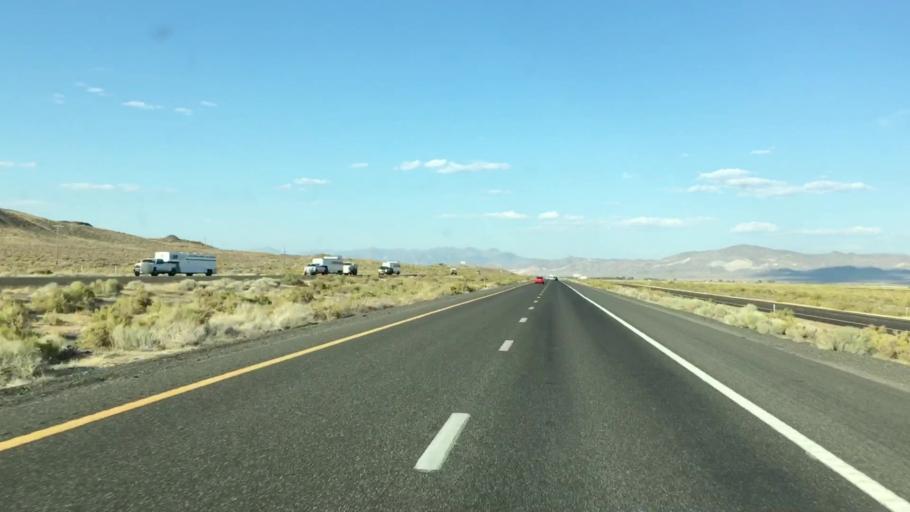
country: US
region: Nevada
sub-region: Pershing County
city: Lovelock
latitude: 40.1176
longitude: -118.5402
